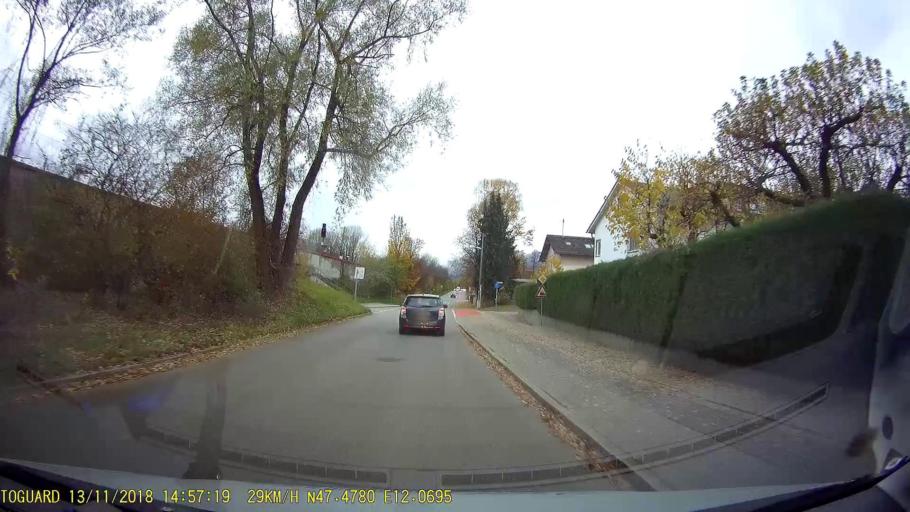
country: DE
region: Bavaria
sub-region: Upper Bavaria
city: Raubling
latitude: 47.7967
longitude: 12.1159
